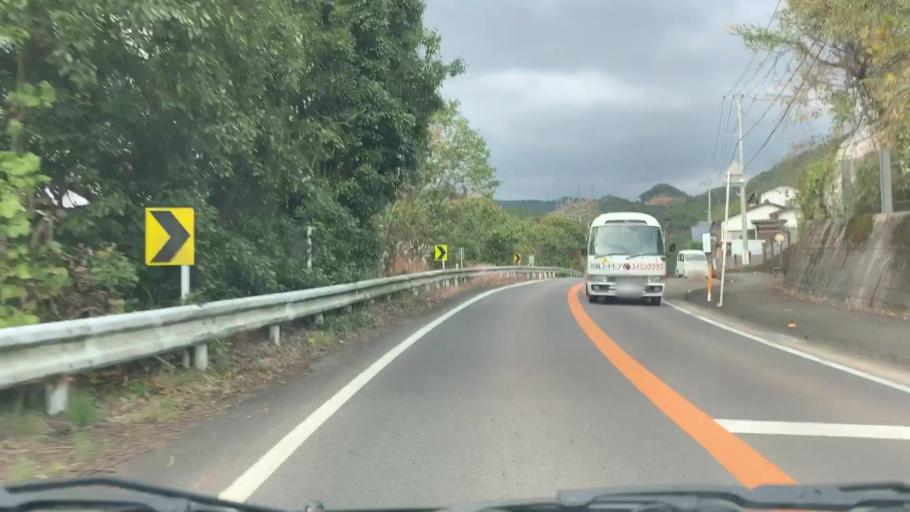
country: JP
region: Saga Prefecture
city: Ureshinomachi-shimojuku
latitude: 33.1319
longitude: 130.0308
